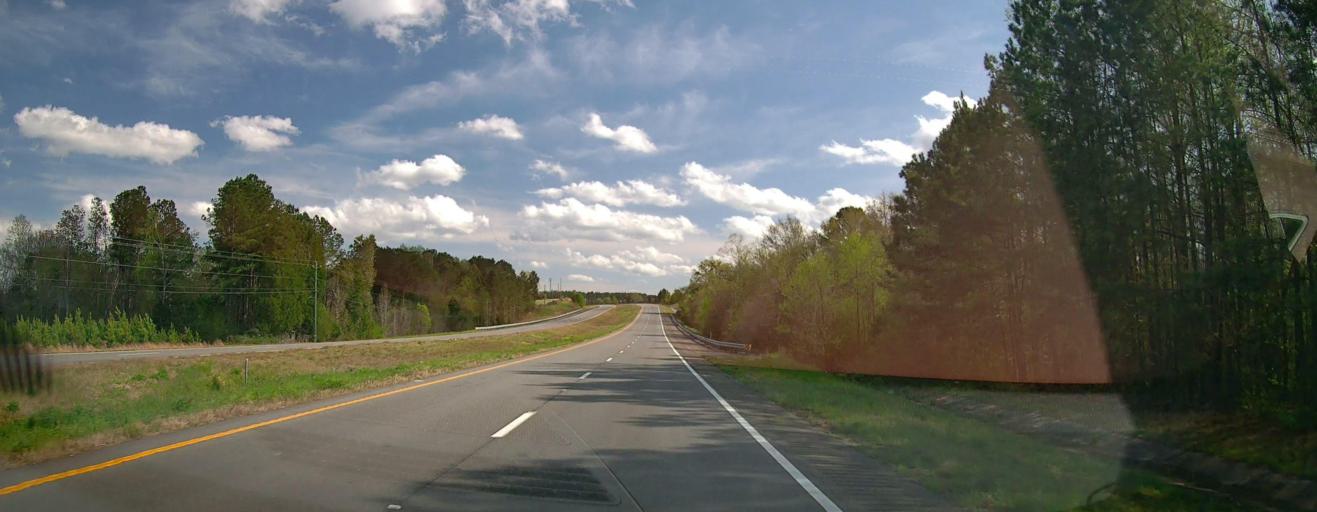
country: US
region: Georgia
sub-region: Baldwin County
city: Hardwick
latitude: 33.0071
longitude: -83.2219
